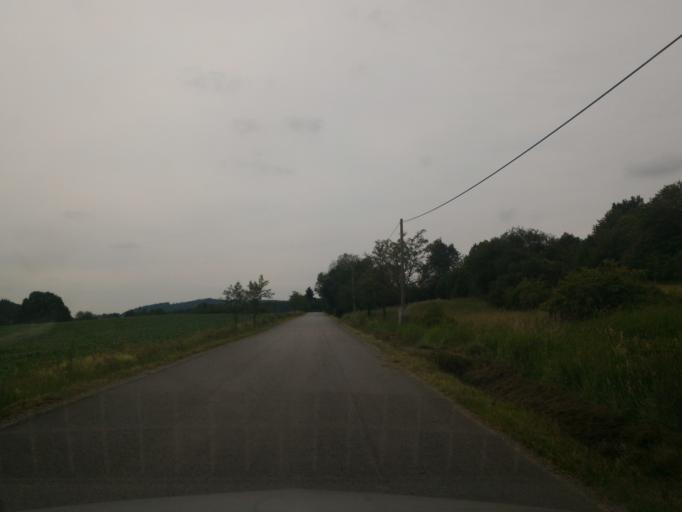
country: CZ
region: Vysocina
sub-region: Okres Jihlava
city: Telc
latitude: 49.1980
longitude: 15.3831
